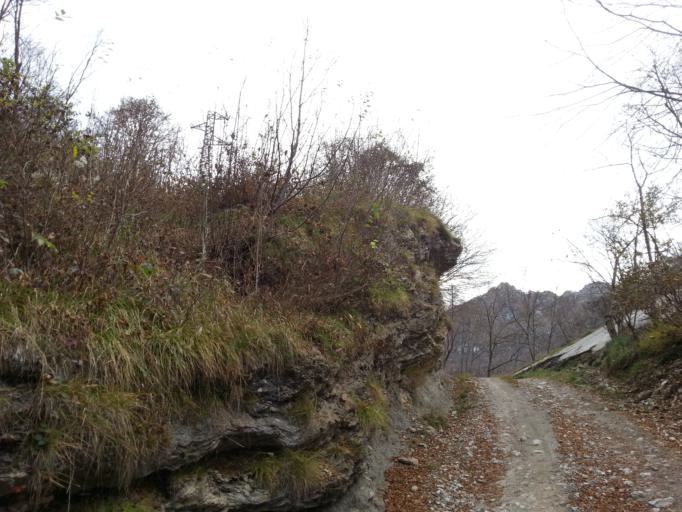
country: IT
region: Lombardy
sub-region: Provincia di Lecco
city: Ballabio
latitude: 45.8821
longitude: 9.4488
